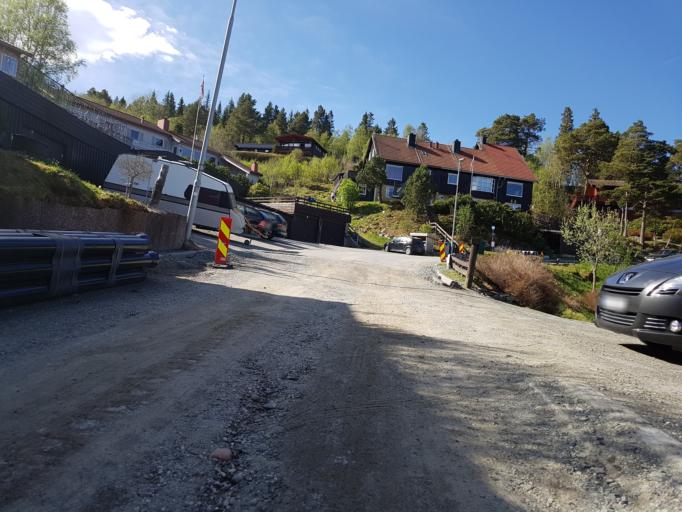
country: NO
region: Sor-Trondelag
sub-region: Trondheim
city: Trondheim
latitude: 63.4497
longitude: 10.3018
